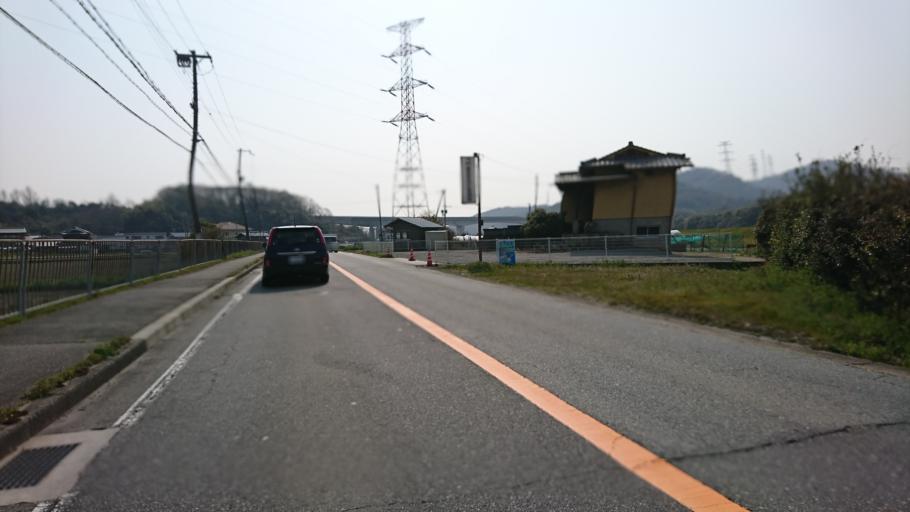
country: JP
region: Hyogo
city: Ono
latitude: 34.8137
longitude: 134.9360
